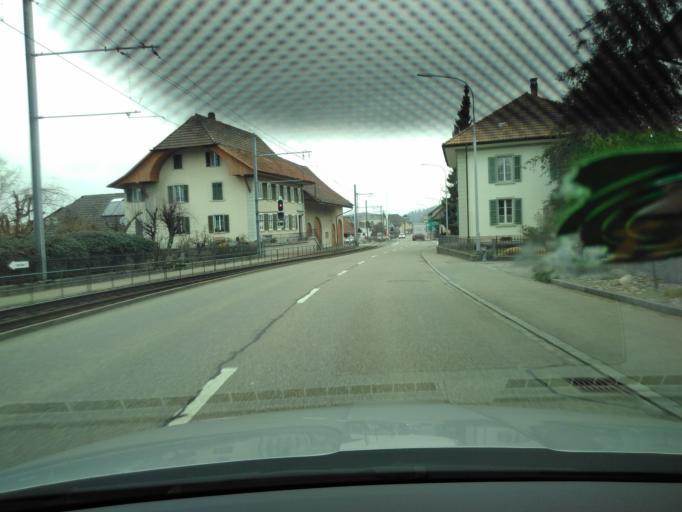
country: CH
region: Aargau
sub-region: Bezirk Kulm
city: Schoftland
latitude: 47.3180
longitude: 8.0526
